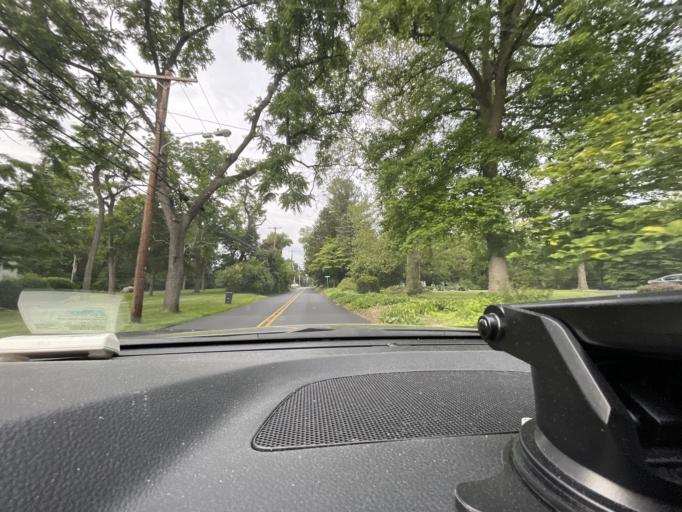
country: US
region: Pennsylvania
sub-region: Montgomery County
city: Plymouth Meeting
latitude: 40.1181
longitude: -75.2961
